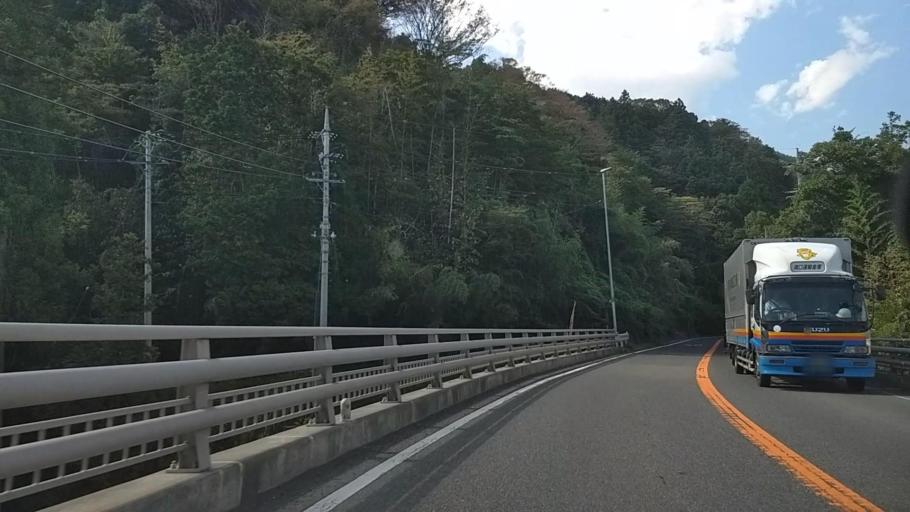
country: JP
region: Shizuoka
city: Fujinomiya
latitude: 35.3908
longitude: 138.4435
